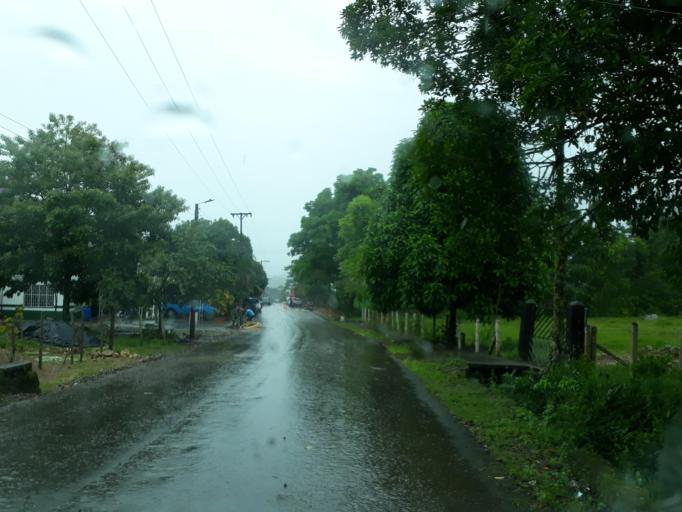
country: CO
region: Cundinamarca
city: Medina
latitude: 4.6472
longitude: -73.3266
